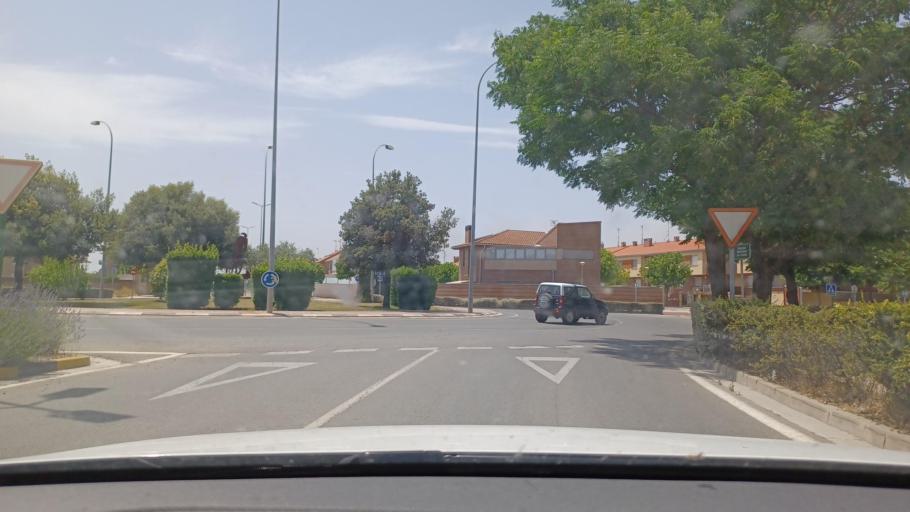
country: ES
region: Navarre
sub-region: Provincia de Navarra
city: Tudela
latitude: 42.0633
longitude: -1.6171
